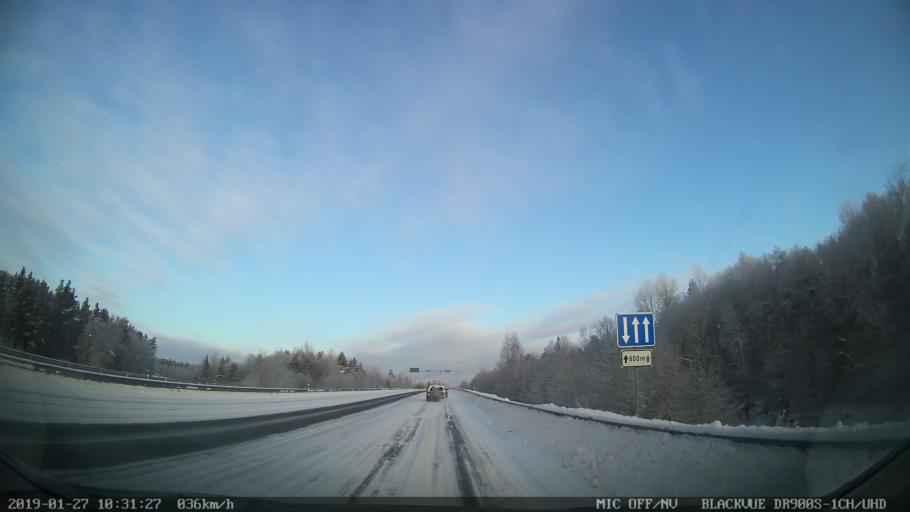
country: EE
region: Harju
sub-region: Raasiku vald
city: Raasiku
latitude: 59.4322
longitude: 25.1919
